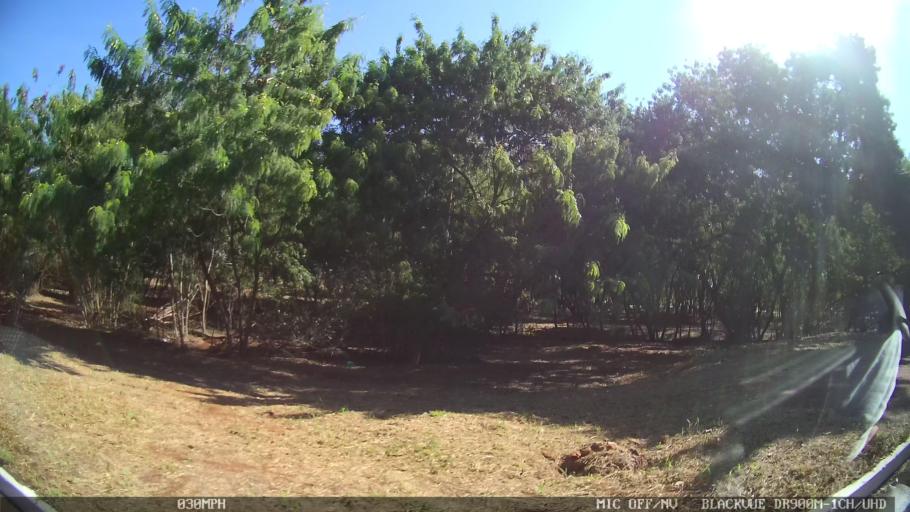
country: BR
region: Sao Paulo
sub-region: Ribeirao Preto
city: Ribeirao Preto
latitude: -21.2243
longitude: -47.7678
